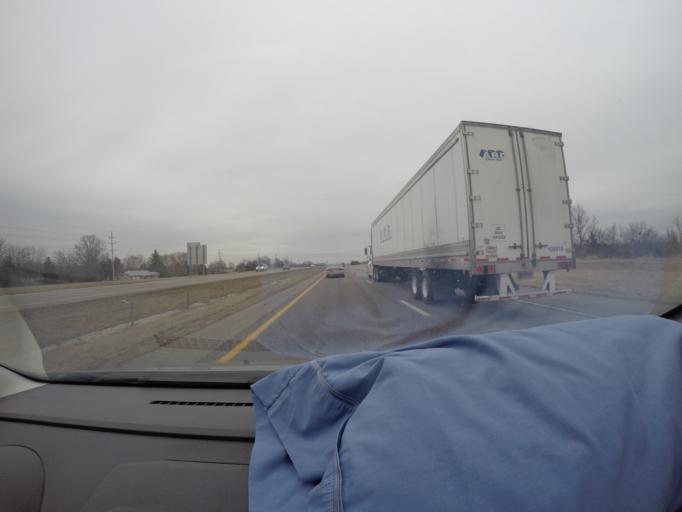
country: US
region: Missouri
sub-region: Saint Charles County
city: Wentzville
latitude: 38.8086
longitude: -90.9233
